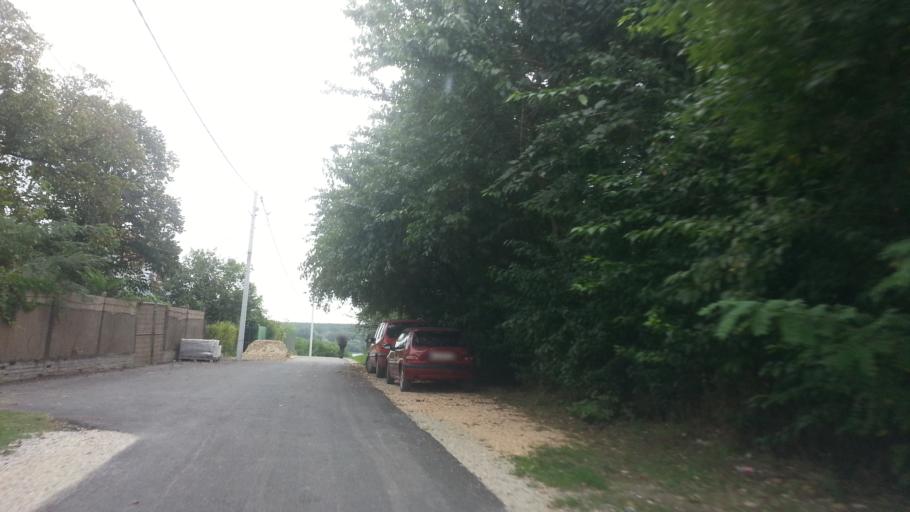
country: RS
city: Stari Banovci
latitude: 44.9805
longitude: 20.2824
